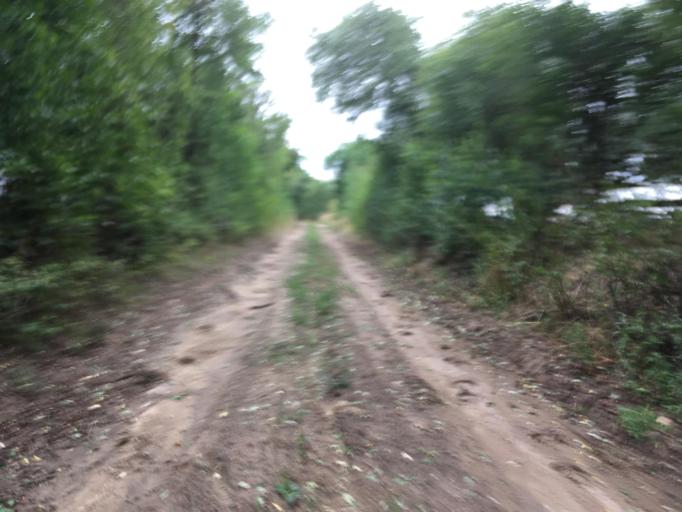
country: DE
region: Brandenburg
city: Passow
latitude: 53.1324
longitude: 14.1103
